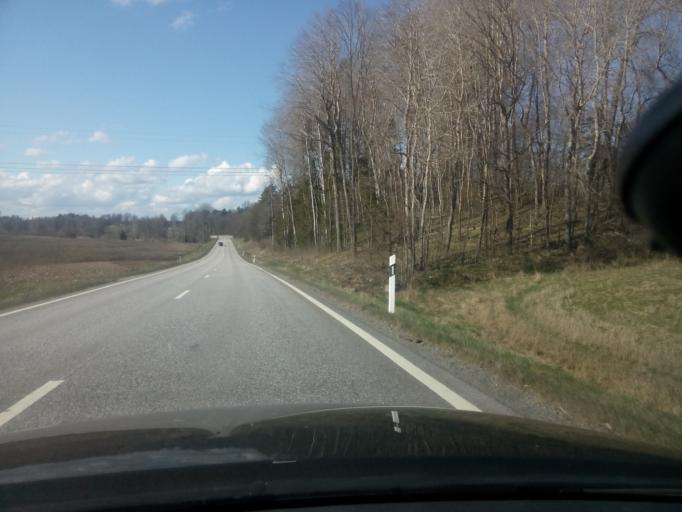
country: SE
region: Soedermanland
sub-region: Flens Kommun
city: Malmkoping
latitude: 59.0906
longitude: 16.8077
